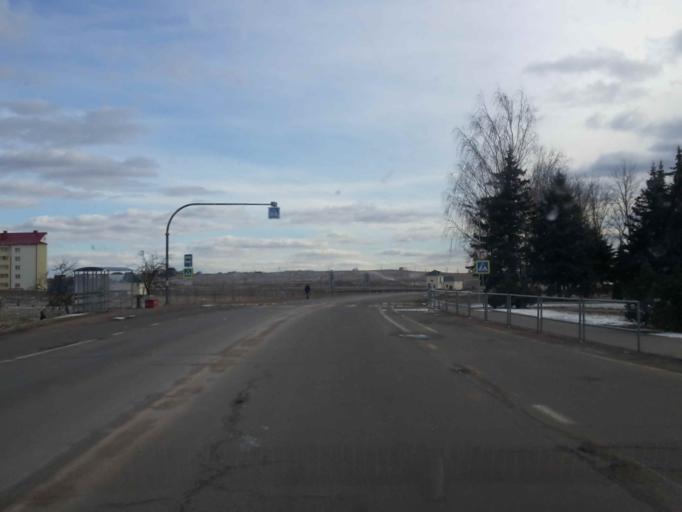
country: BY
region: Minsk
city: Myadzyel
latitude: 54.8765
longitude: 26.9413
